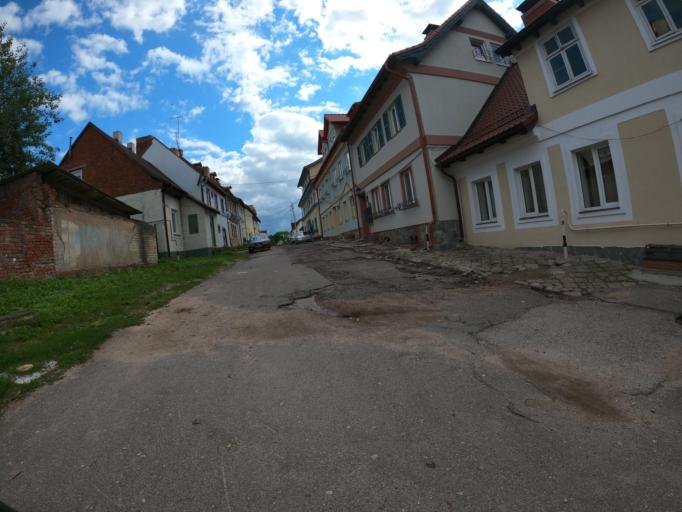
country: RU
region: Kaliningrad
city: Zheleznodorozhnyy
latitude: 54.3617
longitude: 21.3034
